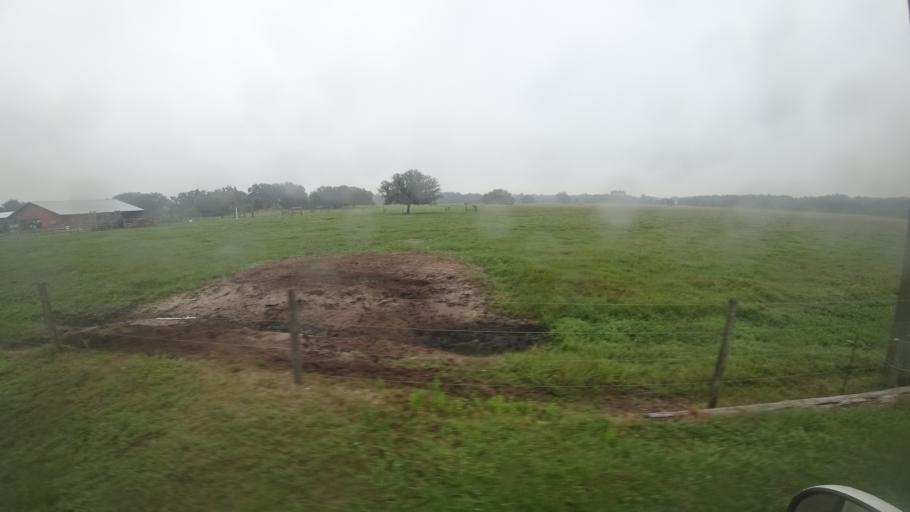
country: US
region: Florida
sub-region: Sarasota County
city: Lake Sarasota
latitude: 27.2916
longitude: -82.2355
